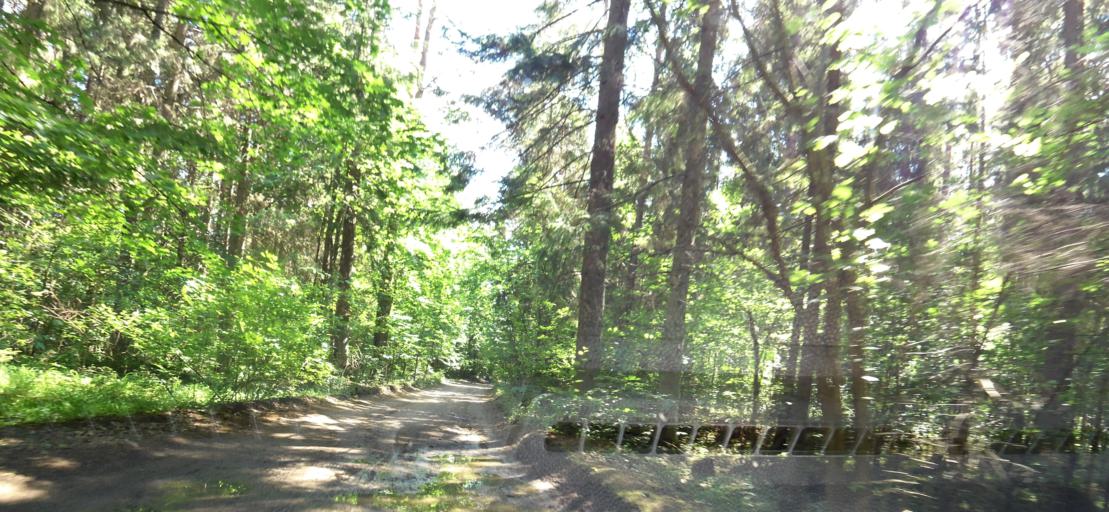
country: LT
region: Vilnius County
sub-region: Vilnius
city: Fabijoniskes
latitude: 54.8271
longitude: 25.3205
